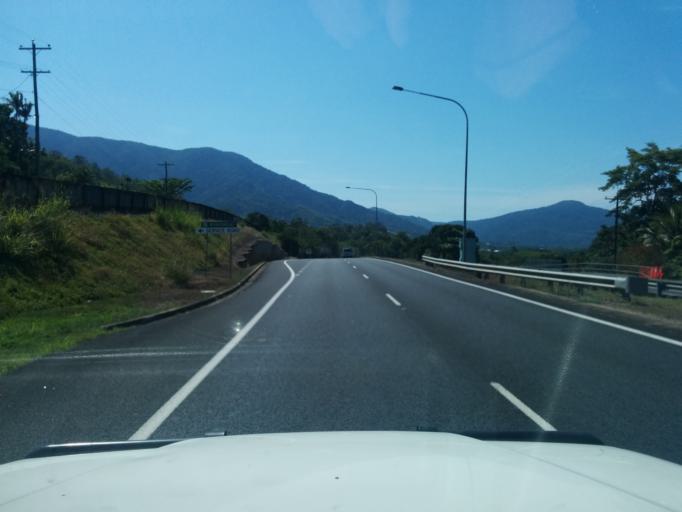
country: AU
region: Queensland
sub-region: Cairns
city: Redlynch
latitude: -16.9104
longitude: 145.7148
